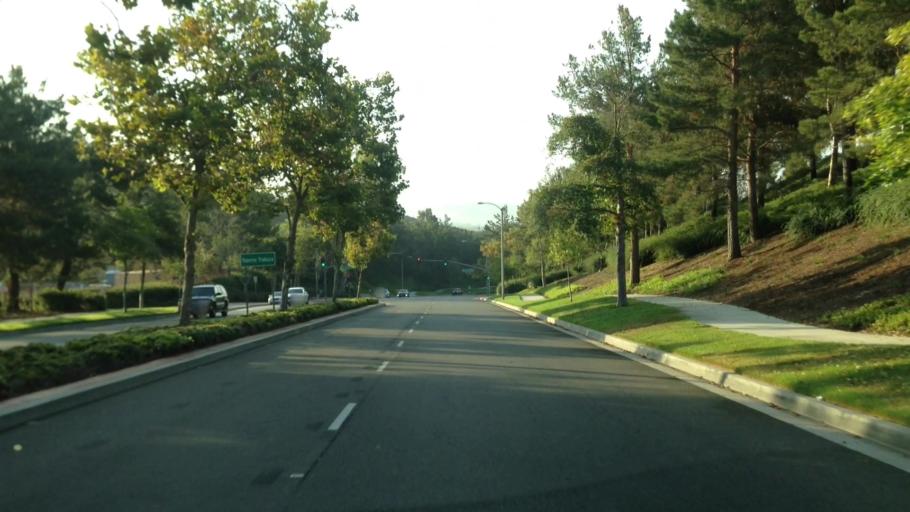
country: US
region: California
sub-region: Orange County
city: Rancho Santa Margarita
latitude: 33.6572
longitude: -117.6156
